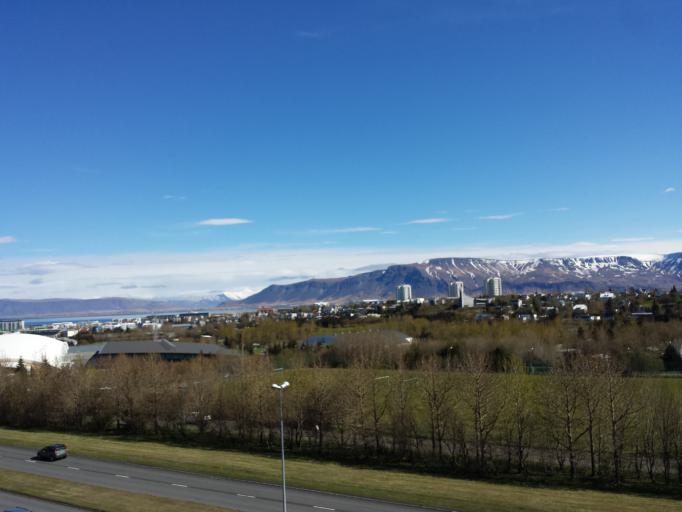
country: IS
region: Capital Region
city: Reykjavik
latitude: 64.1372
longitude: -21.8767
